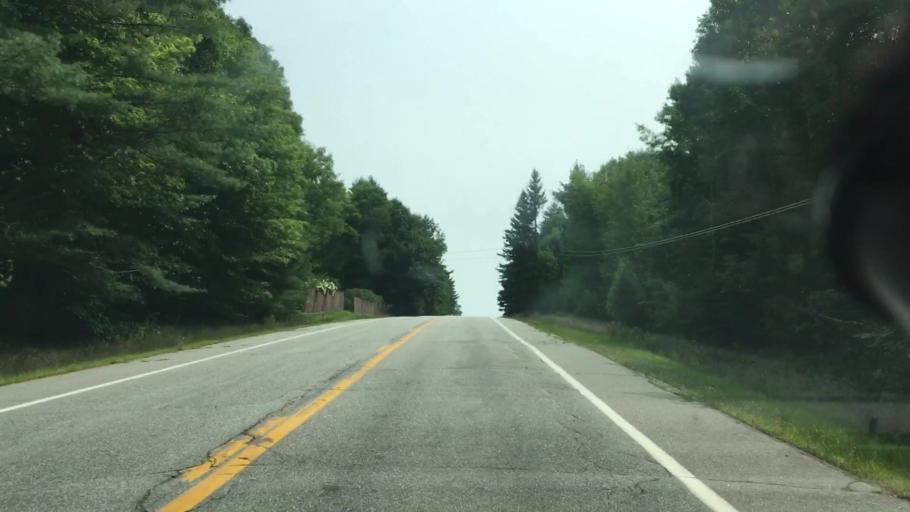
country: US
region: Maine
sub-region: Kennebec County
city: Wayne
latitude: 44.3991
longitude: -70.1228
